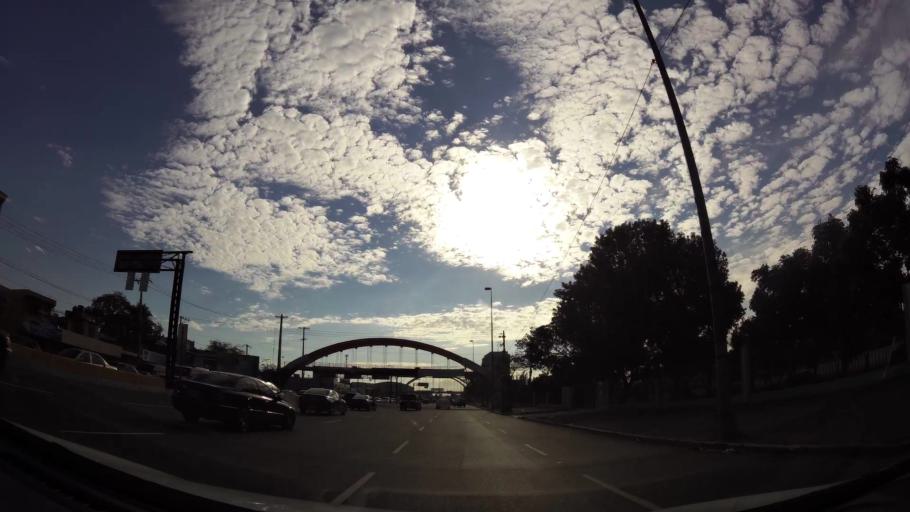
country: DO
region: Nacional
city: San Carlos
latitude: 18.4819
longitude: -69.9180
